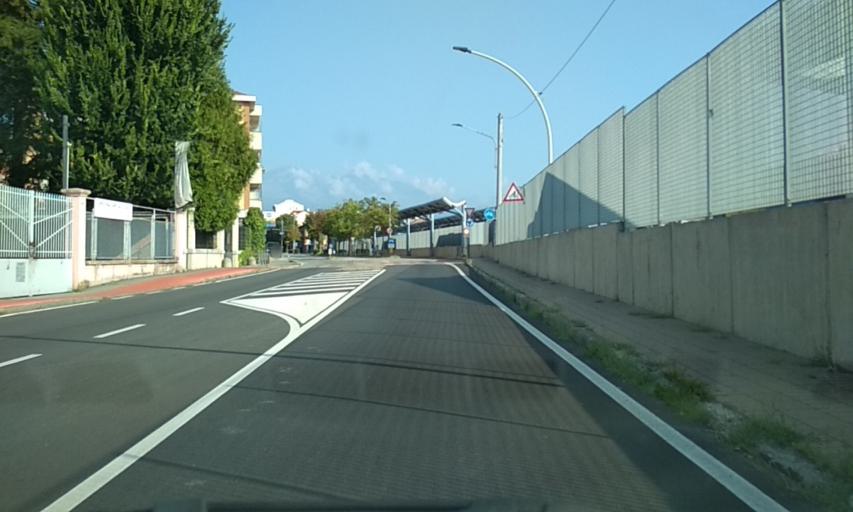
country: IT
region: Piedmont
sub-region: Provincia di Torino
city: Rivarolo Canavese
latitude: 45.3266
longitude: 7.7271
